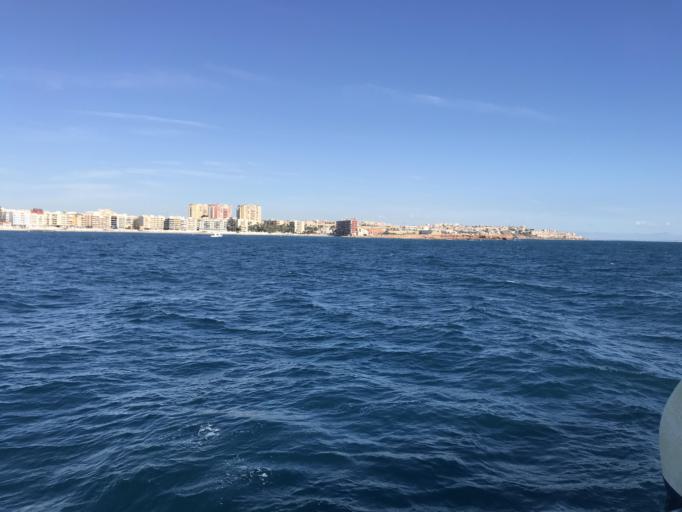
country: ES
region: Valencia
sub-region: Provincia de Alicante
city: Torrevieja
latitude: 37.9762
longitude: -0.6562
